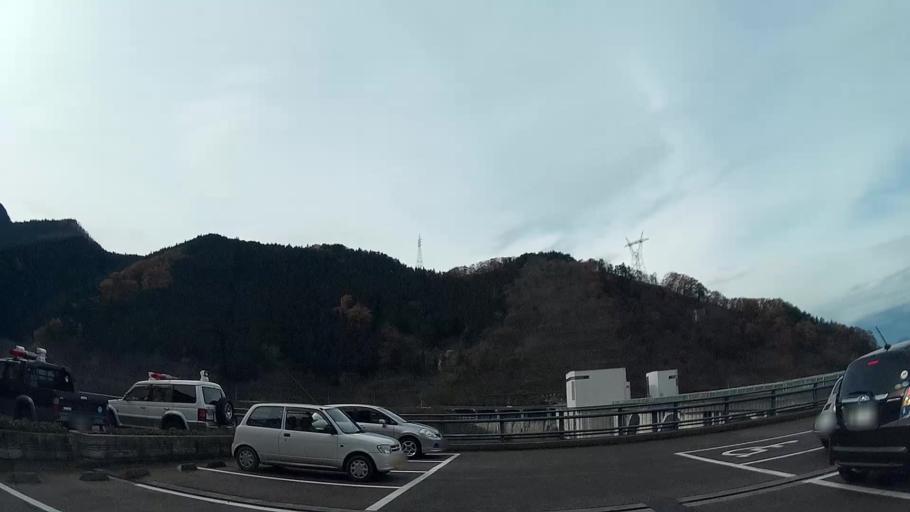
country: JP
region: Saitama
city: Chichibu
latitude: 35.9528
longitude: 139.0543
